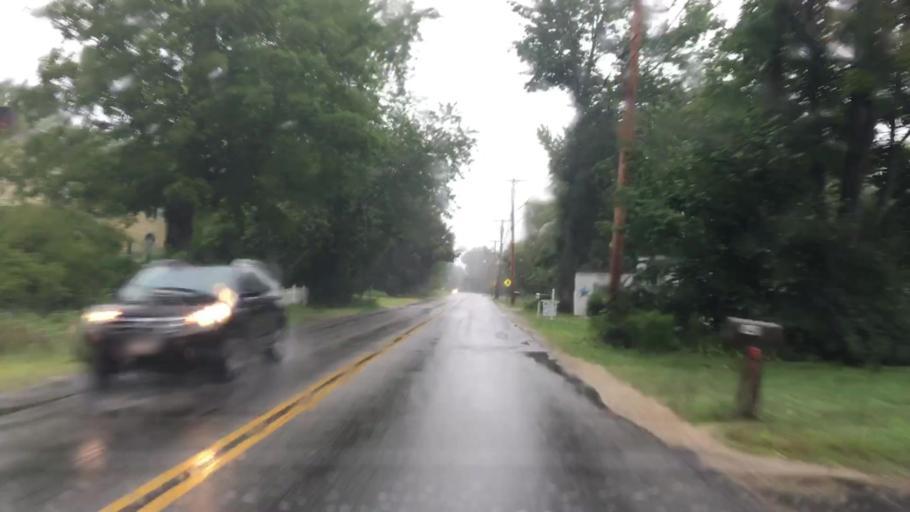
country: US
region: Maine
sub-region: Cumberland County
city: Bridgton
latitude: 44.0440
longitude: -70.7115
